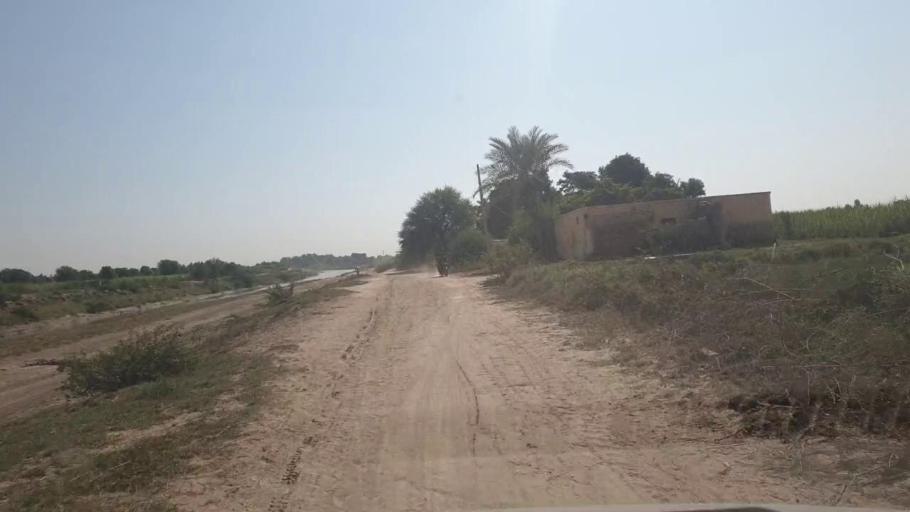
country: PK
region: Sindh
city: Tando Bago
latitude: 24.7635
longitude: 69.1540
